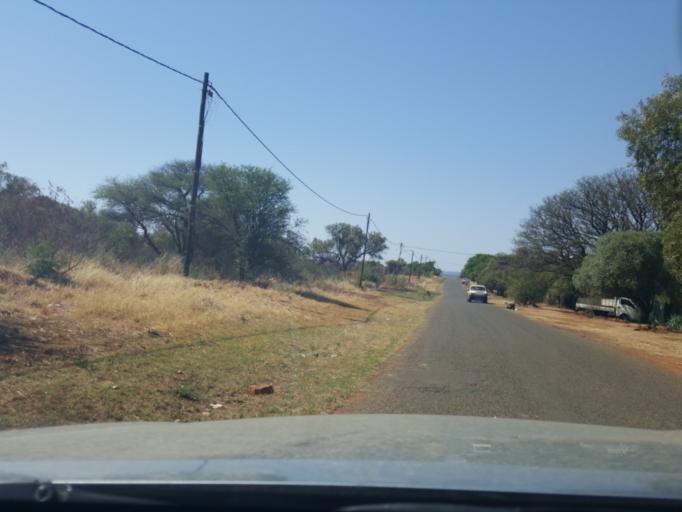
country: ZA
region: North-West
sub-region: Ngaka Modiri Molema District Municipality
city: Zeerust
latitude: -25.5280
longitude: 26.0806
